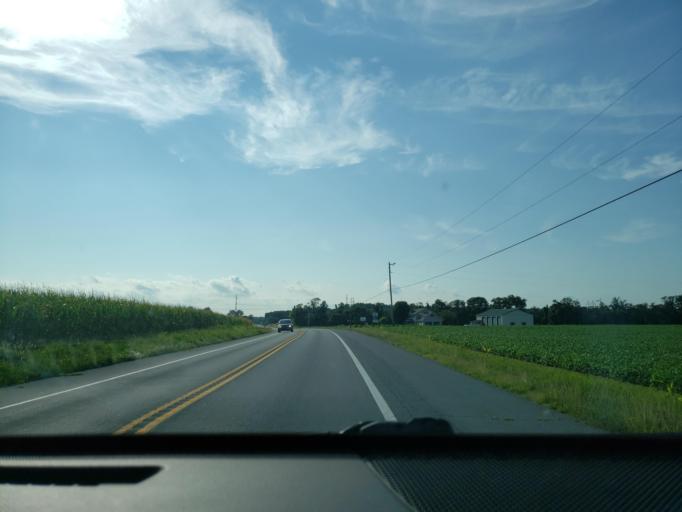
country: US
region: Delaware
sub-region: Sussex County
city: Milton
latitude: 38.7633
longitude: -75.2710
